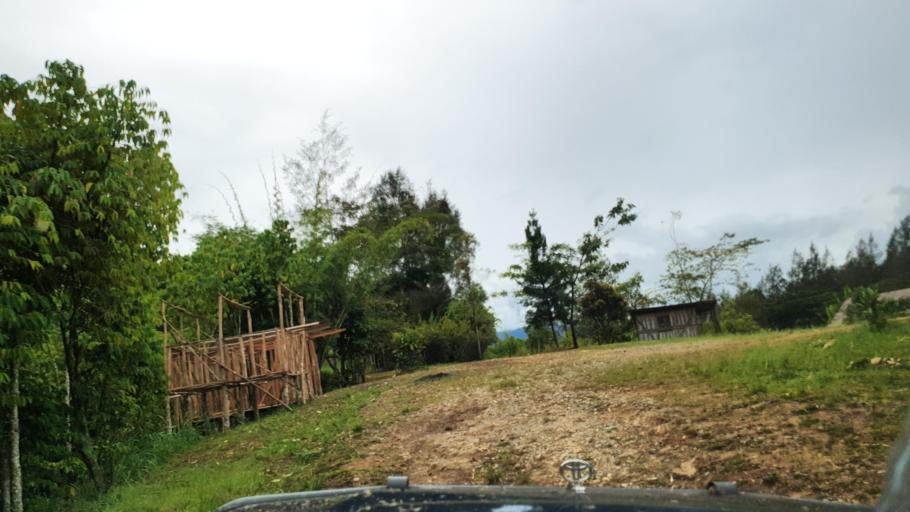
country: PG
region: Jiwaka
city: Minj
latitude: -5.9313
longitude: 144.7529
